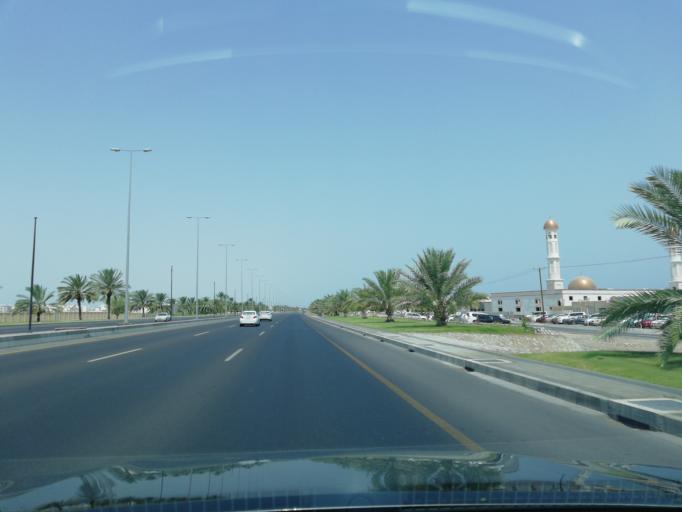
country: OM
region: Muhafazat Masqat
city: As Sib al Jadidah
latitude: 23.6796
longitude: 58.1178
